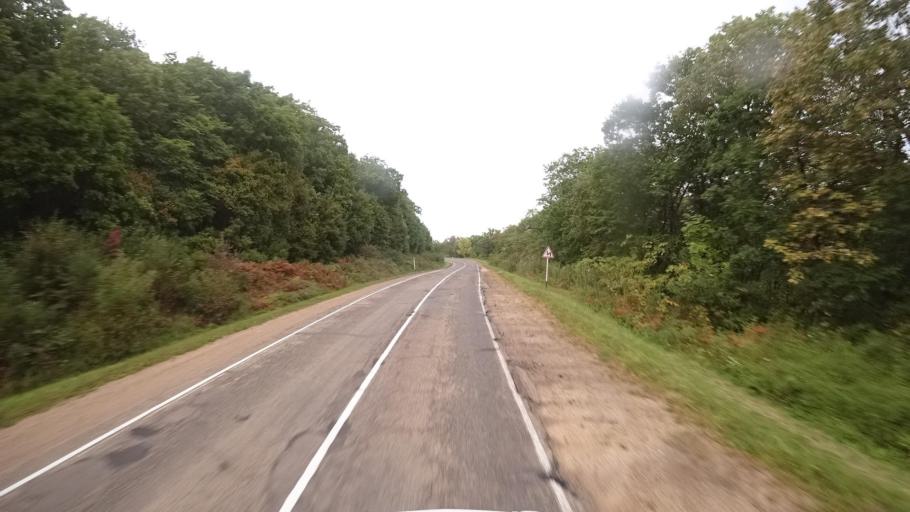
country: RU
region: Primorskiy
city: Yakovlevka
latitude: 44.3908
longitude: 133.4681
